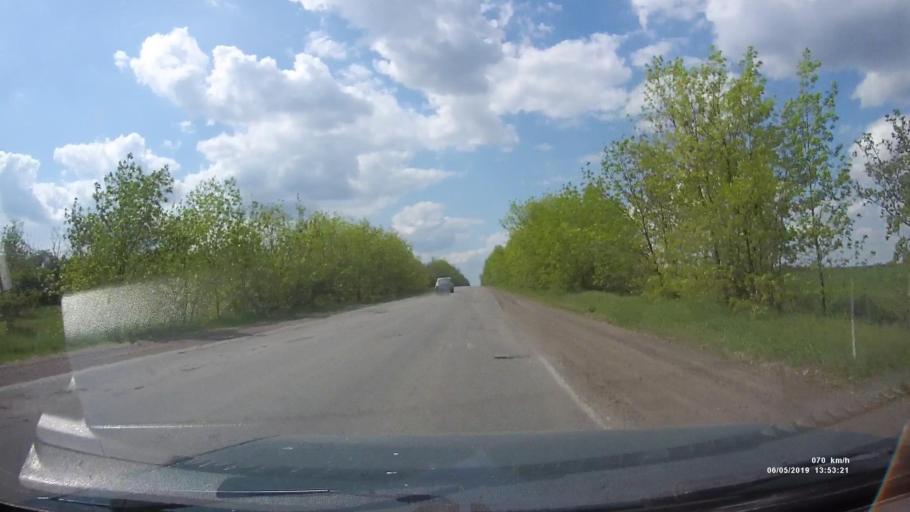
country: RU
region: Rostov
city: Melikhovskaya
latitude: 47.6677
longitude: 40.4636
